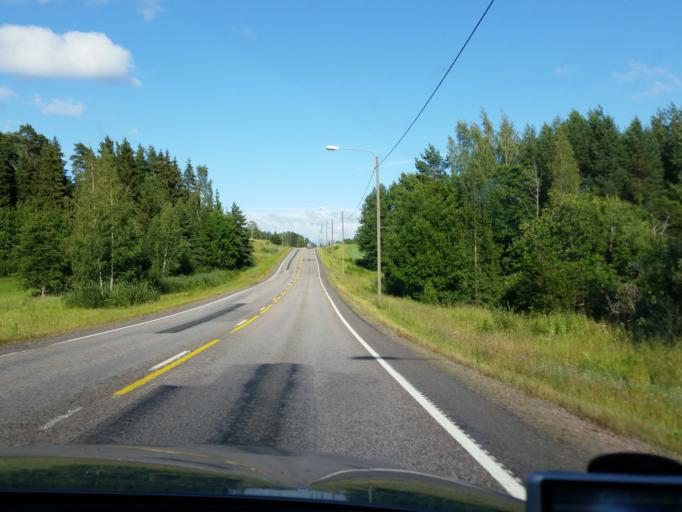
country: FI
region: Uusimaa
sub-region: Helsinki
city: Lohja
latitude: 60.3705
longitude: 24.1287
